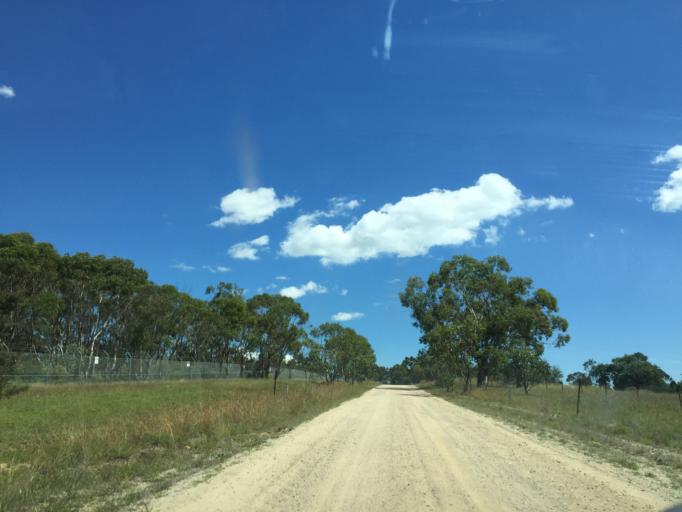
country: AU
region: New South Wales
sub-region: Lithgow
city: Lithgow
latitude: -33.4337
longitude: 150.1335
